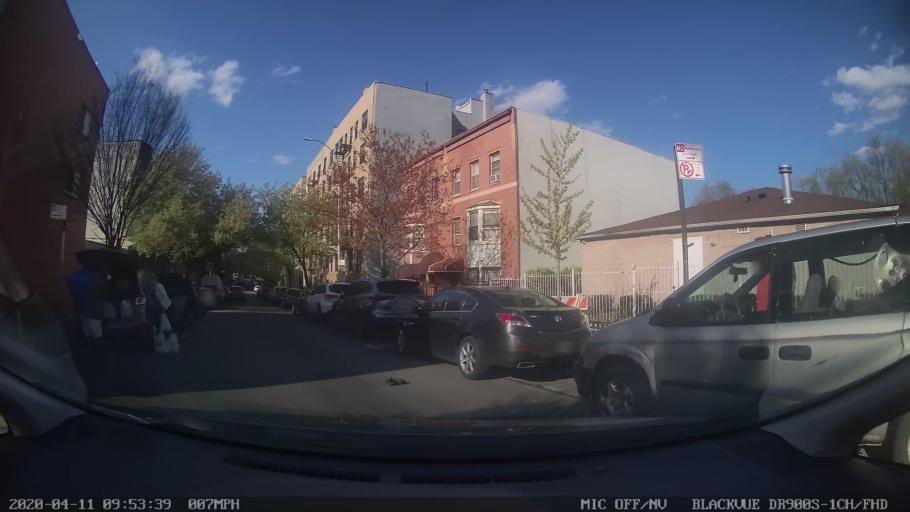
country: US
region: New York
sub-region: New York County
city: Inwood
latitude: 40.8428
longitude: -73.9062
